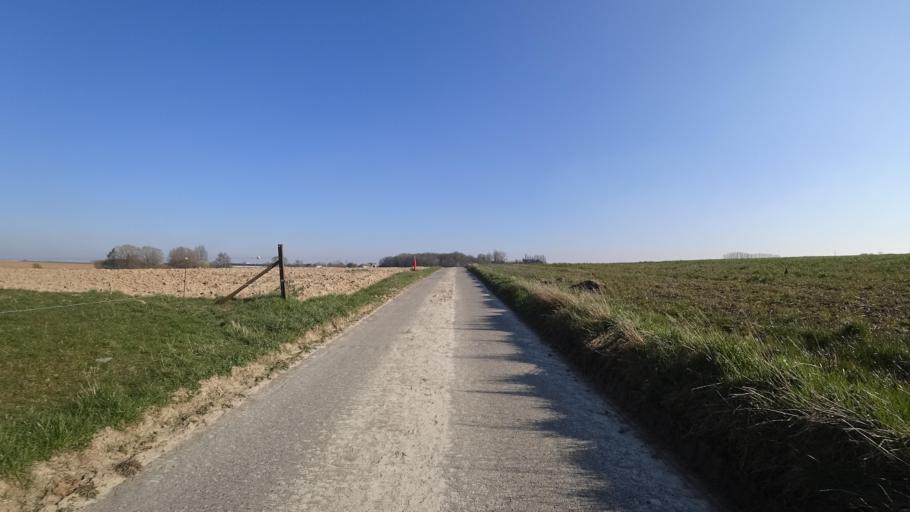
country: BE
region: Wallonia
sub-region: Province du Brabant Wallon
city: Chastre
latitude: 50.5674
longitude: 4.6580
